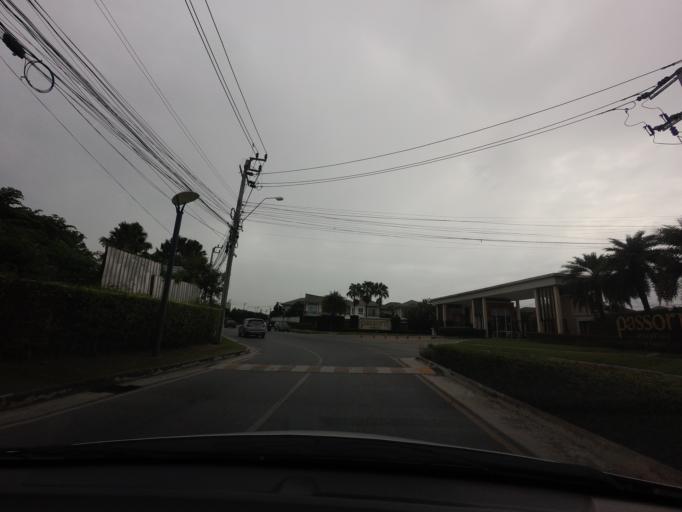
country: TH
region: Bangkok
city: Suan Luang
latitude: 13.7228
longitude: 100.6294
